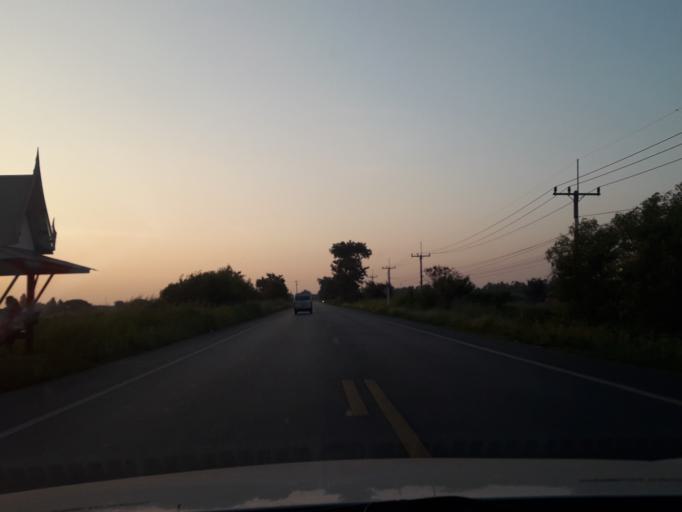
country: TH
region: Phra Nakhon Si Ayutthaya
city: Maha Rat
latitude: 14.5241
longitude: 100.5382
